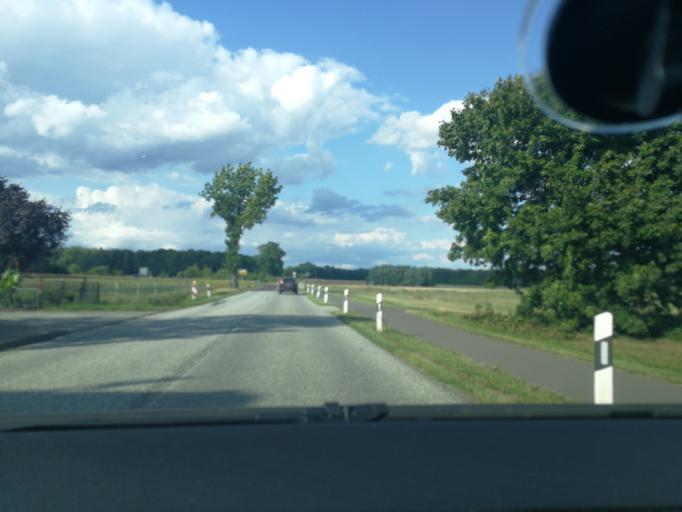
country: DE
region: Brandenburg
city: Pritzwalk
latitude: 53.1624
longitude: 12.1829
